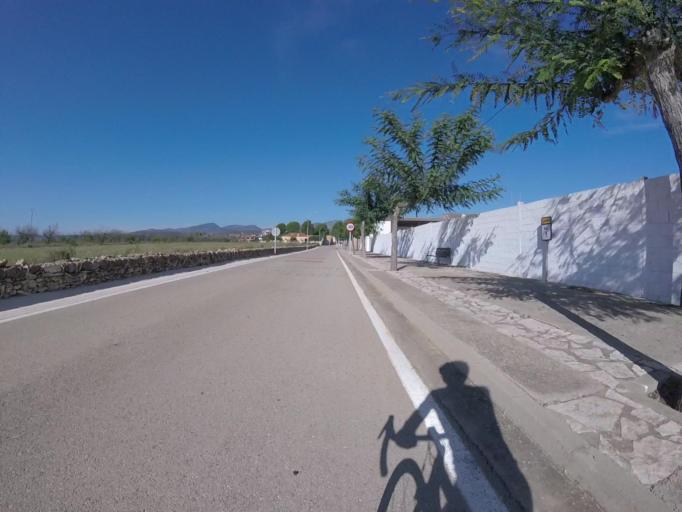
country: ES
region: Valencia
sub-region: Provincia de Castello
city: Sarratella
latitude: 40.2616
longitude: 0.0741
